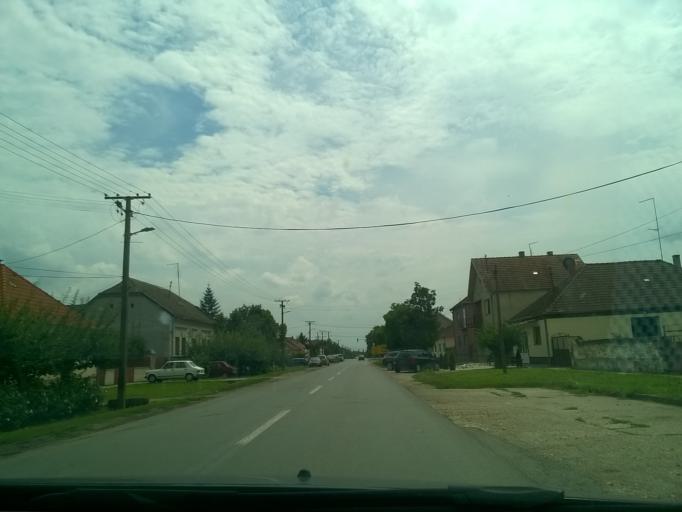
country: RS
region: Autonomna Pokrajina Vojvodina
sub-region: Juznobanatski Okrug
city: Plandiste
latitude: 45.2279
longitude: 21.1207
